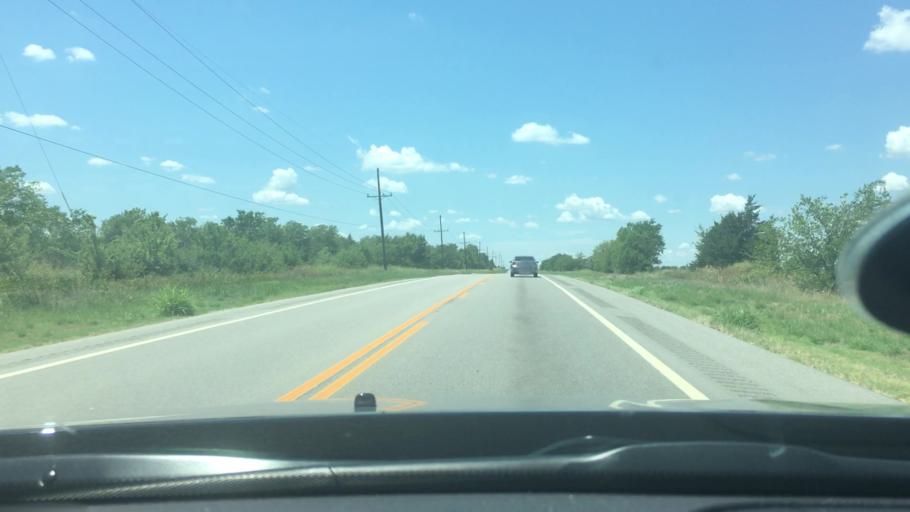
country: US
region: Oklahoma
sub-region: Bryan County
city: Durant
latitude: 34.0026
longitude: -96.2046
